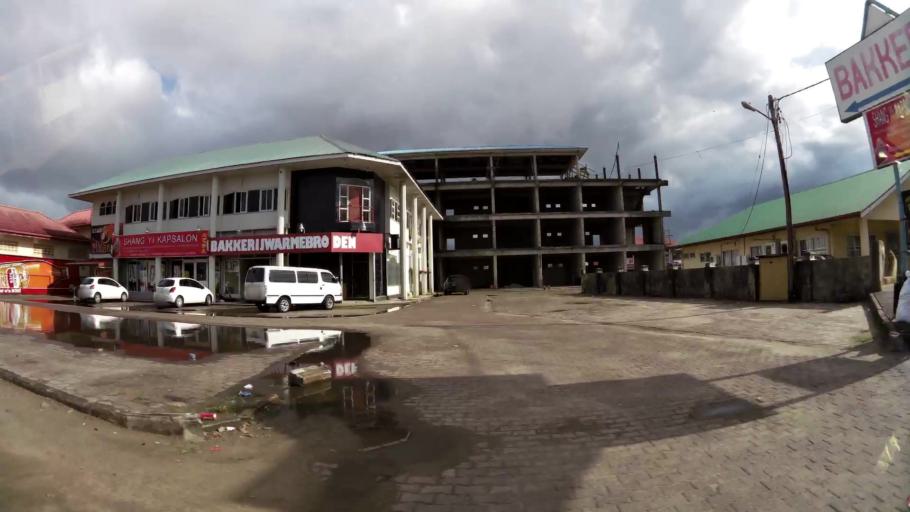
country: SR
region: Paramaribo
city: Paramaribo
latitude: 5.8443
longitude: -55.2191
